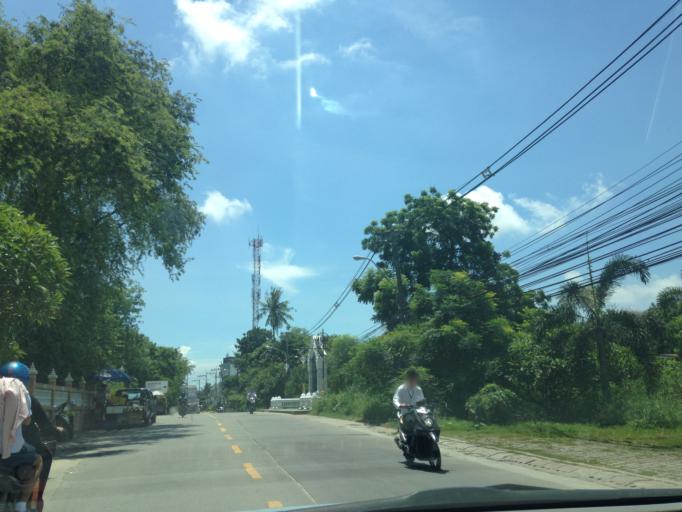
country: TH
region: Chon Buri
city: Chon Buri
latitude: 13.2947
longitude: 100.9369
